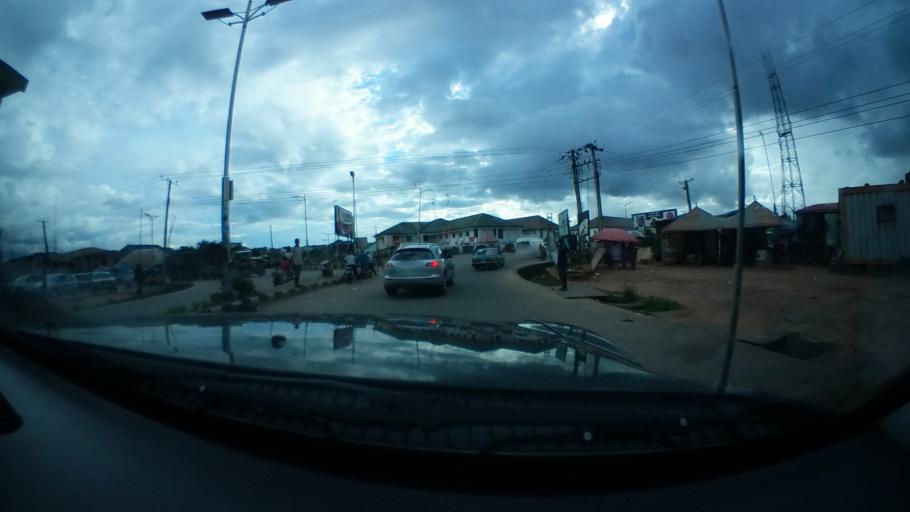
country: NG
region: Imo
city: Orlu
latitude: 5.7979
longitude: 7.0368
